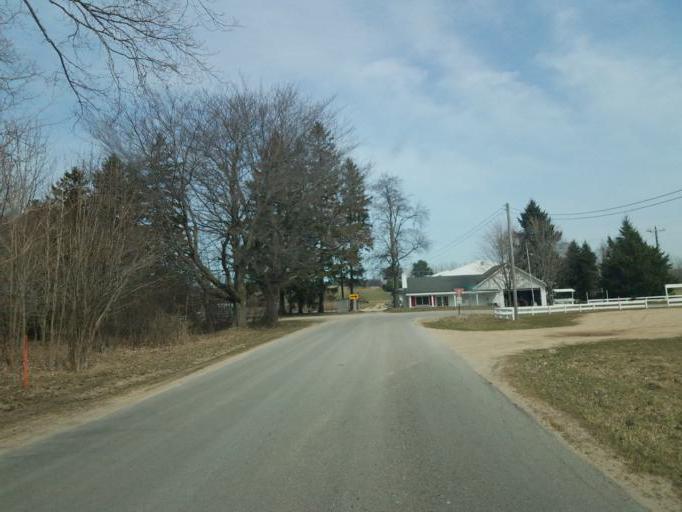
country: US
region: Michigan
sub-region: Oceana County
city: Shelby
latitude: 43.6306
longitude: -86.5180
